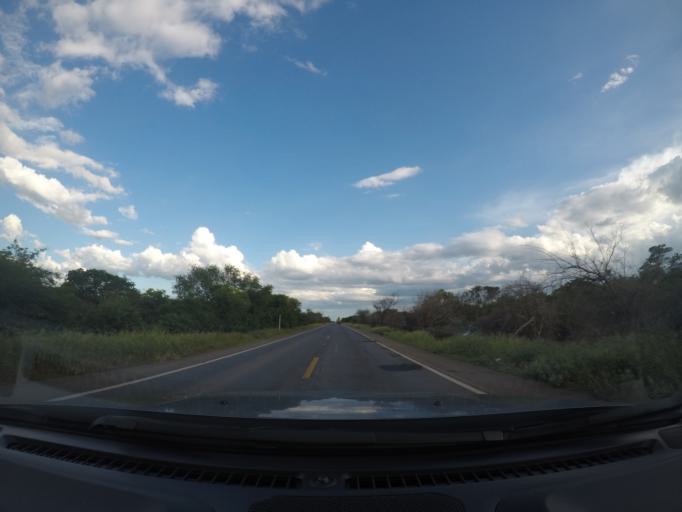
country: BR
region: Bahia
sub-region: Oliveira Dos Brejinhos
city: Beira Rio
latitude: -12.2054
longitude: -42.8081
